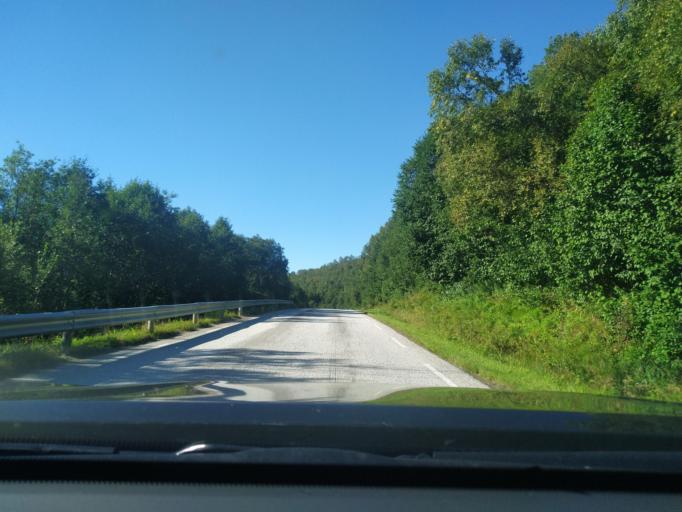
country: NO
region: Troms
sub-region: Dyroy
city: Brostadbotn
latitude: 68.9284
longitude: 17.6465
